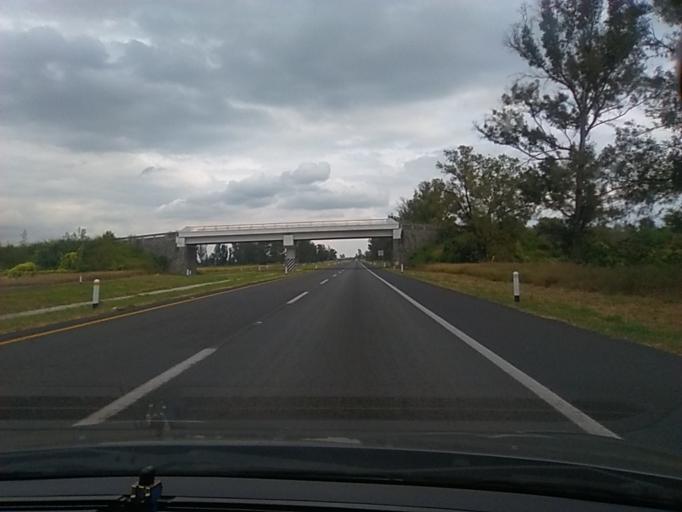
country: MX
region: Jalisco
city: Ocotlan
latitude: 20.3873
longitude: -102.7116
